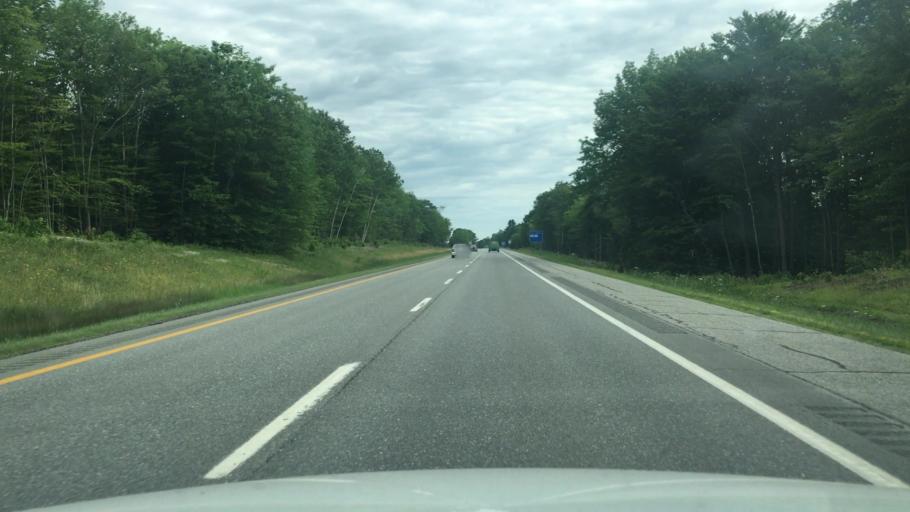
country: US
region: Maine
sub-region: Kennebec County
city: Oakland
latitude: 44.5332
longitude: -69.6885
